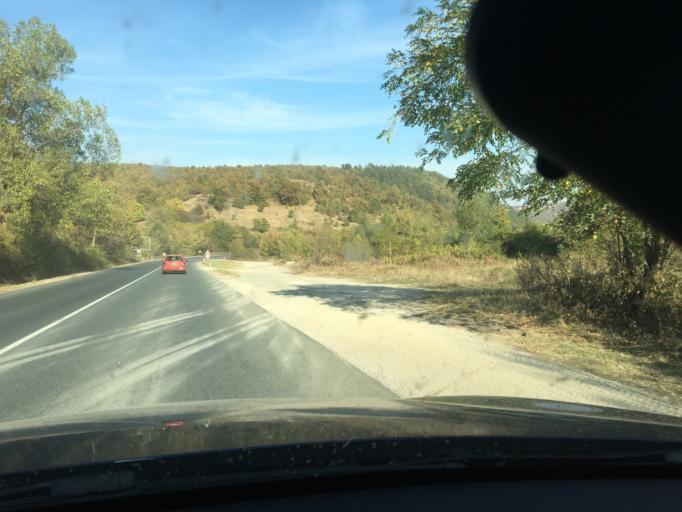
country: BG
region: Lovech
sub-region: Obshtina Yablanitsa
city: Yablanitsa
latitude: 43.0578
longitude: 24.2273
